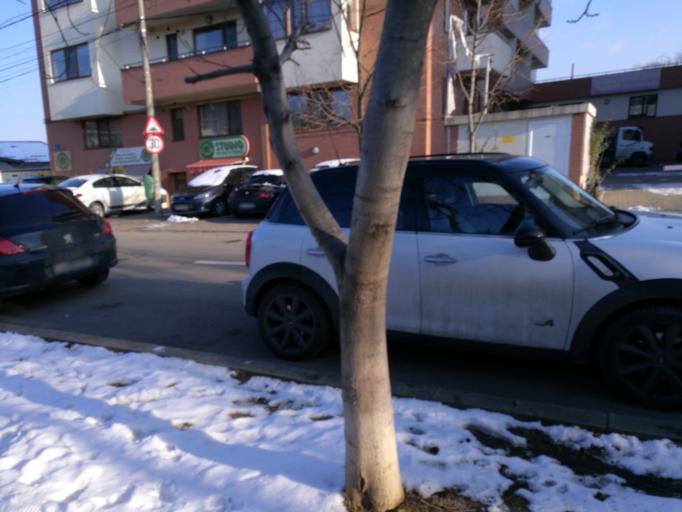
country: RO
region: Ilfov
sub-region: Comuna Otopeni
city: Otopeni
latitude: 44.5034
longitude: 26.0598
